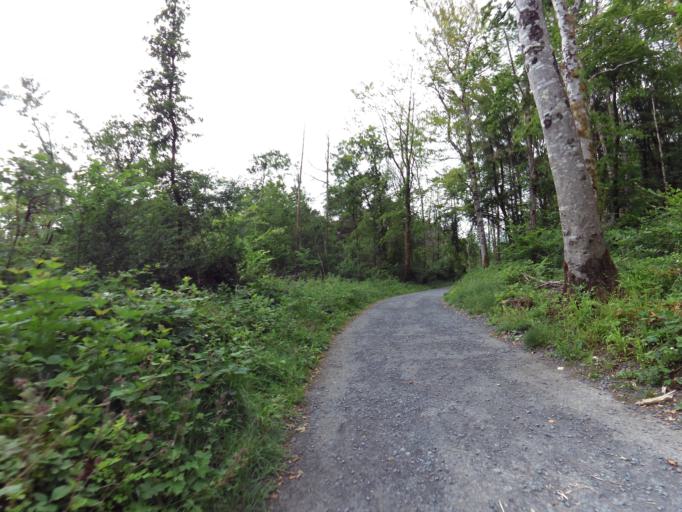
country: IE
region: Connaught
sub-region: County Galway
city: Gort
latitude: 53.0849
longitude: -8.8465
